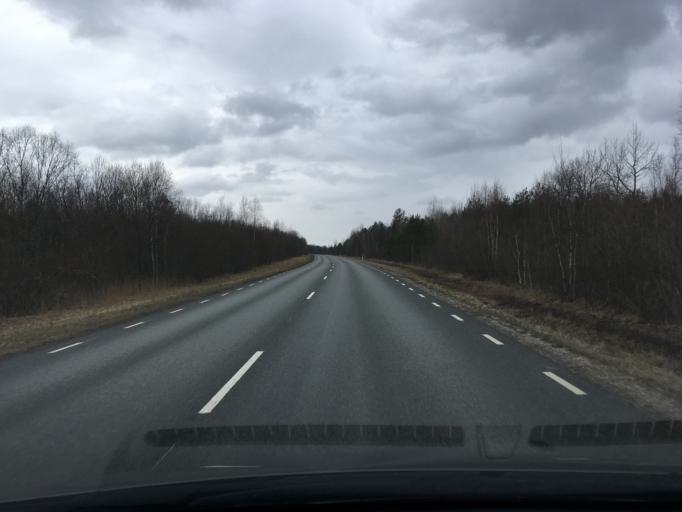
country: EE
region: Laeaene
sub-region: Lihula vald
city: Lihula
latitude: 58.6235
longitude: 23.8966
